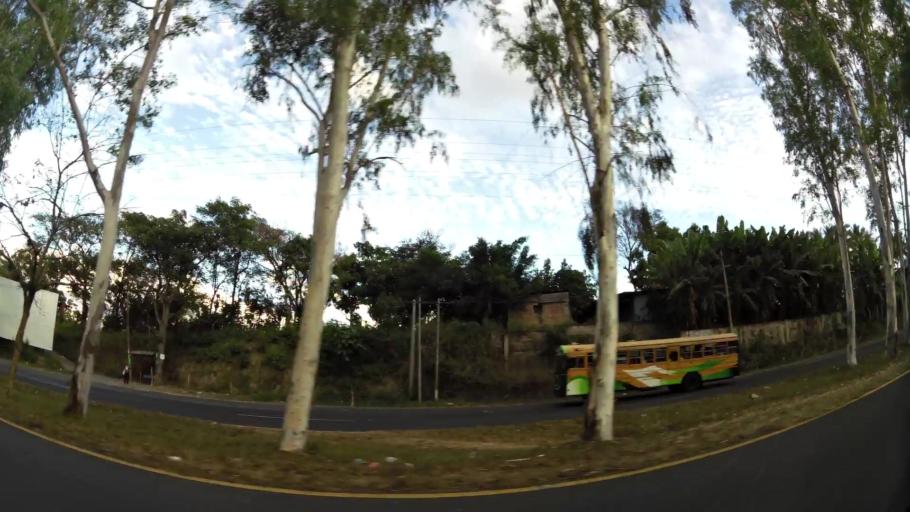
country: SV
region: San Vicente
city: San Sebastian
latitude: 13.6917
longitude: -88.8477
